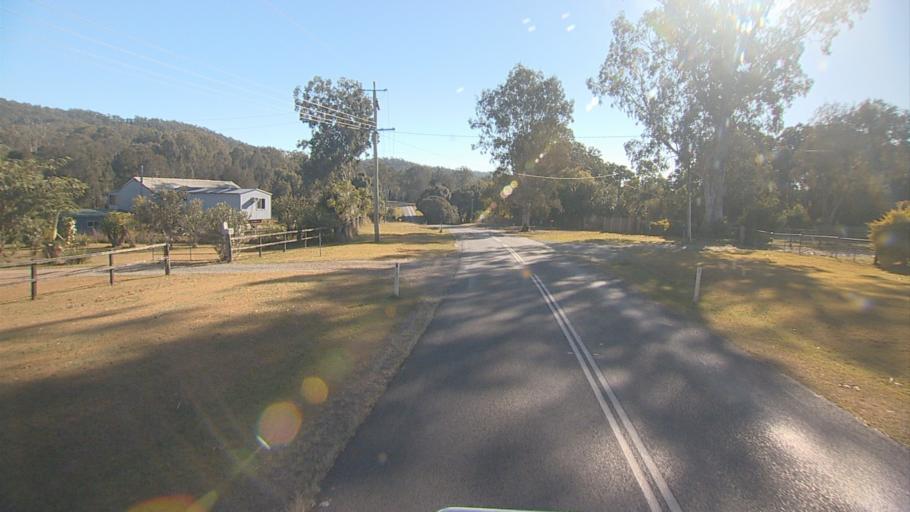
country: AU
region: Queensland
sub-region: Logan
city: Windaroo
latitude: -27.8099
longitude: 153.1707
